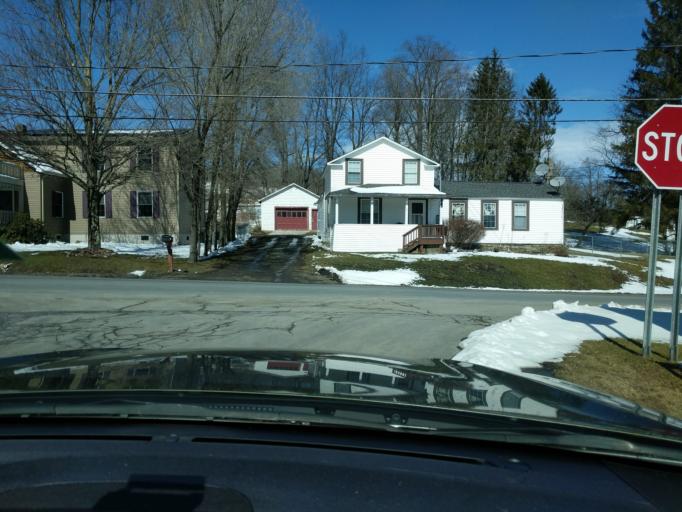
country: US
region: New York
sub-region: Tompkins County
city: Dryden
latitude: 42.3043
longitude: -76.2533
